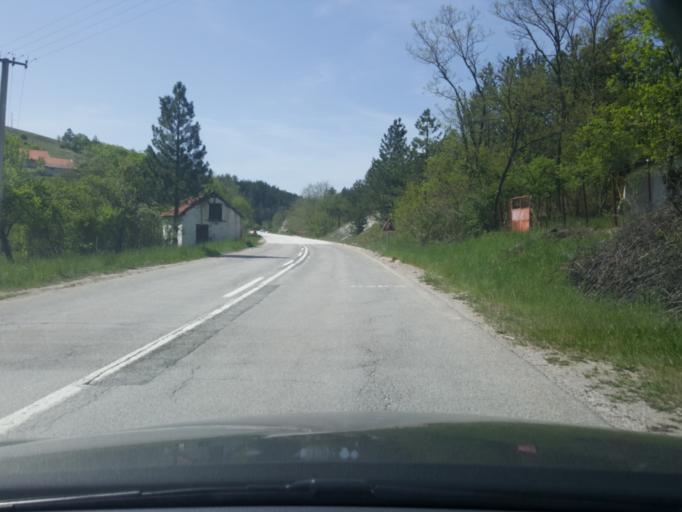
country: RS
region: Central Serbia
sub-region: Zlatiborski Okrug
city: Cajetina
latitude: 43.7899
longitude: 19.6614
